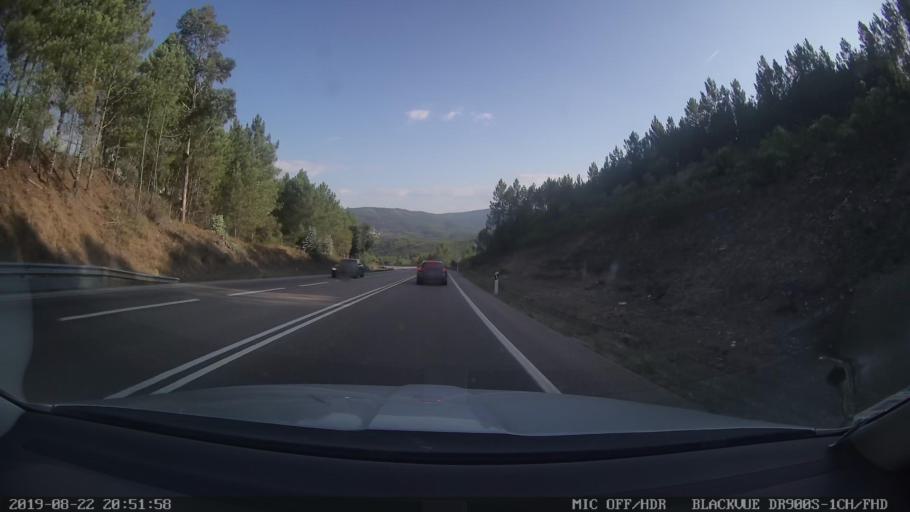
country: PT
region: Castelo Branco
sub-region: Proenca-A-Nova
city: Proenca-a-Nova
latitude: 39.7646
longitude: -7.9669
